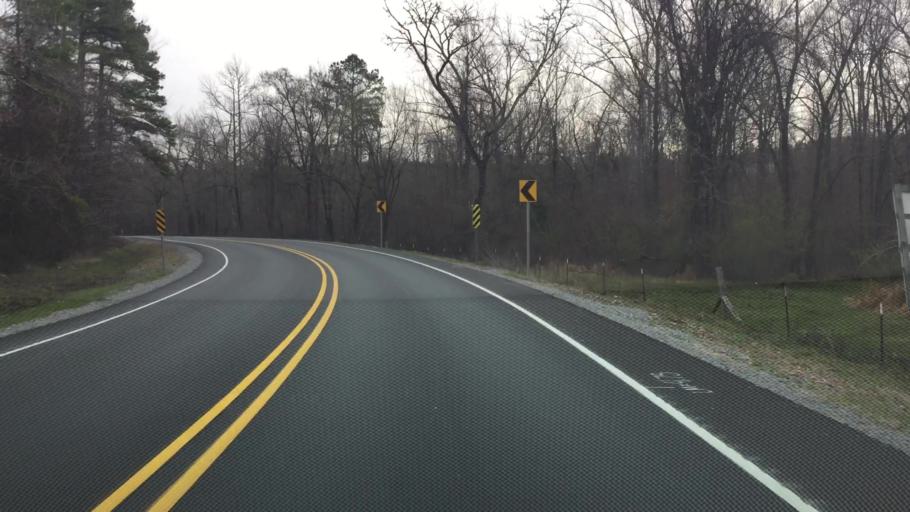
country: US
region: Arkansas
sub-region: Saline County
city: Haskell
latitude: 34.6122
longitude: -92.7962
